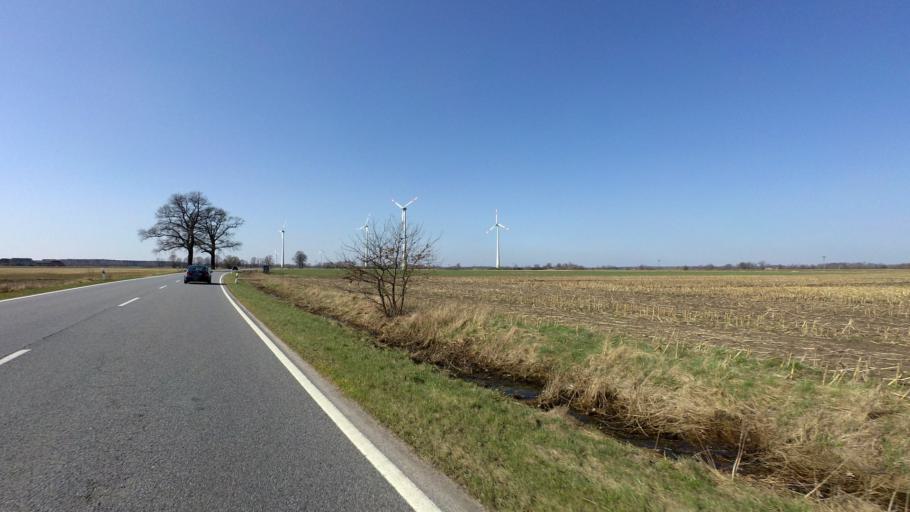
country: DE
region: Brandenburg
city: Ruthnick
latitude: 52.9011
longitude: 13.0274
